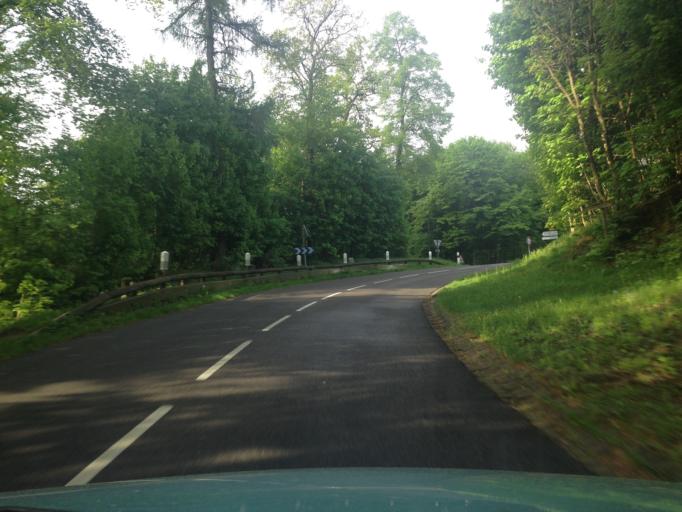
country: FR
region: Alsace
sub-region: Departement du Bas-Rhin
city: Neuwiller-les-Saverne
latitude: 48.8582
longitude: 7.3405
